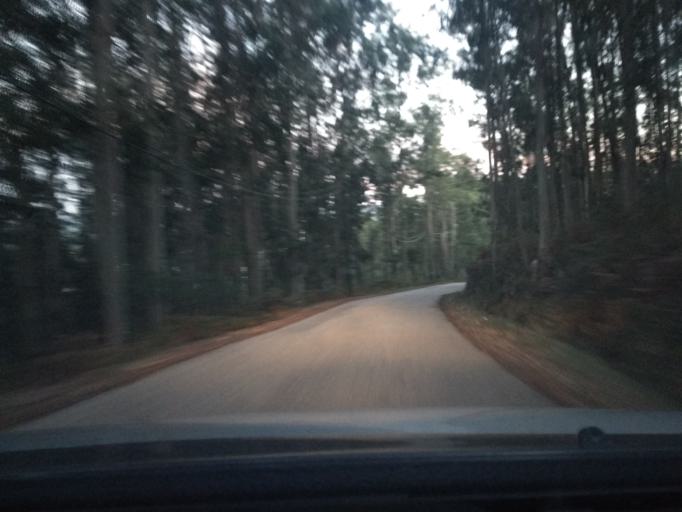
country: ES
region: Galicia
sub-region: Provincia de Pontevedra
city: Moana
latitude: 42.2993
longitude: -8.6955
